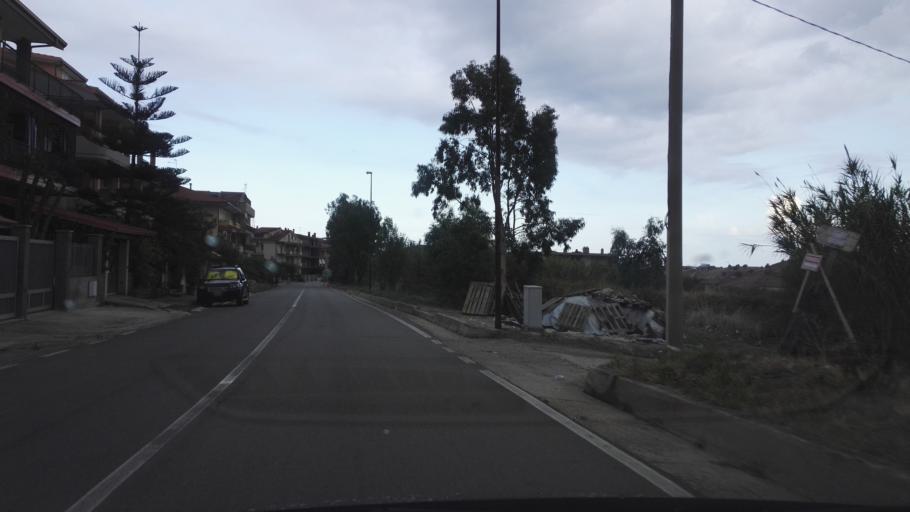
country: IT
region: Calabria
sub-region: Provincia di Catanzaro
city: Badolato Marina
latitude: 38.5719
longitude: 16.5601
